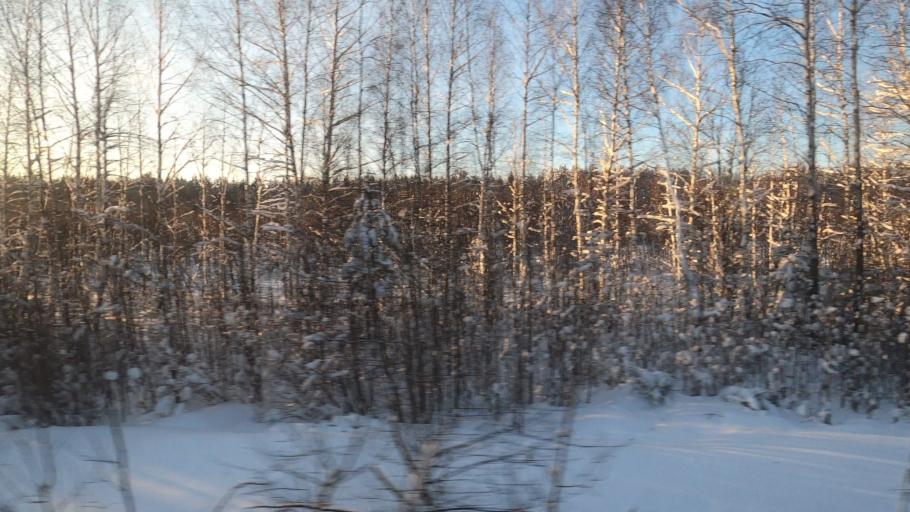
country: RU
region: Moskovskaya
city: Taldom
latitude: 56.6547
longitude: 37.5664
